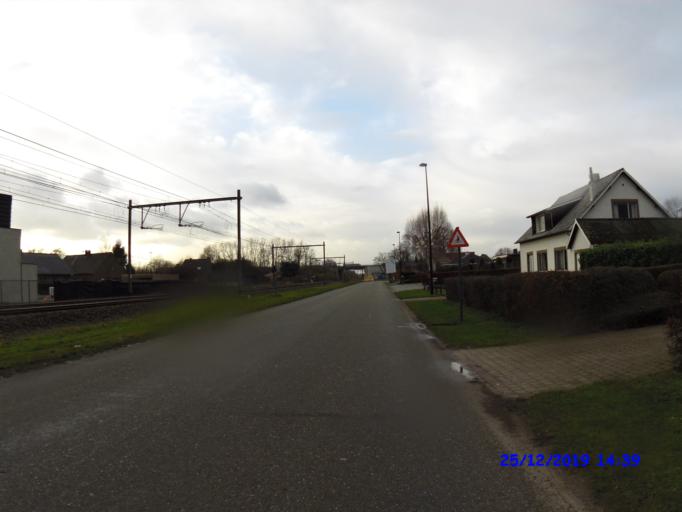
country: BE
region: Flanders
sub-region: Provincie Antwerpen
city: Geel
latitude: 51.1681
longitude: 4.9688
